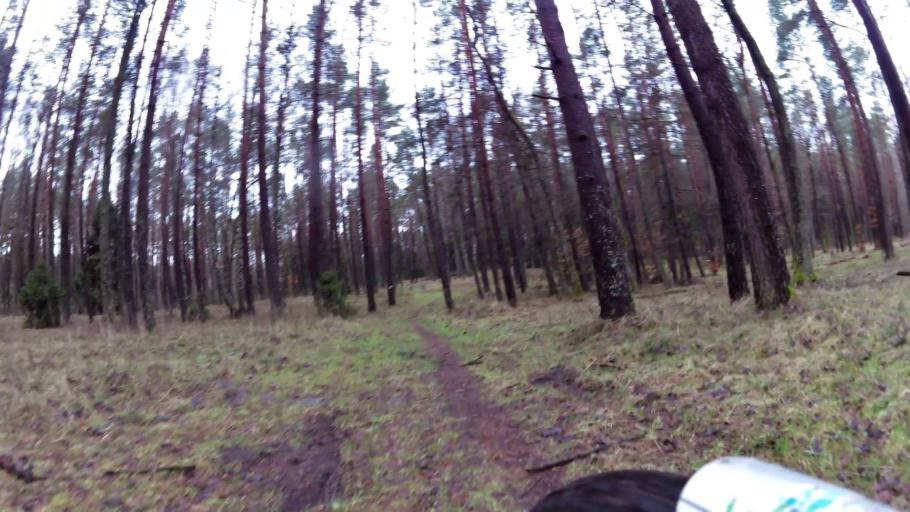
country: PL
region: Pomeranian Voivodeship
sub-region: Powiat bytowski
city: Borzytuchom
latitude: 54.2700
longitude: 17.4147
